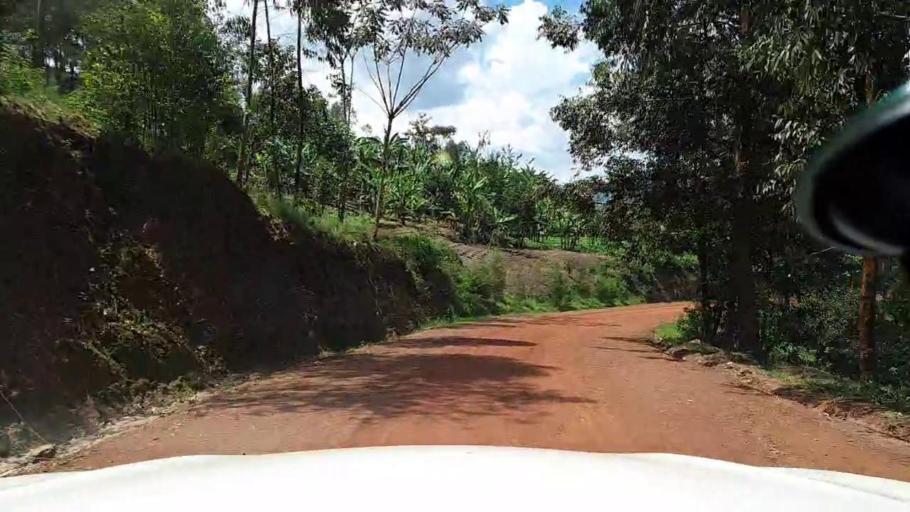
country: RW
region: Northern Province
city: Musanze
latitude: -1.6907
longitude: 29.8242
